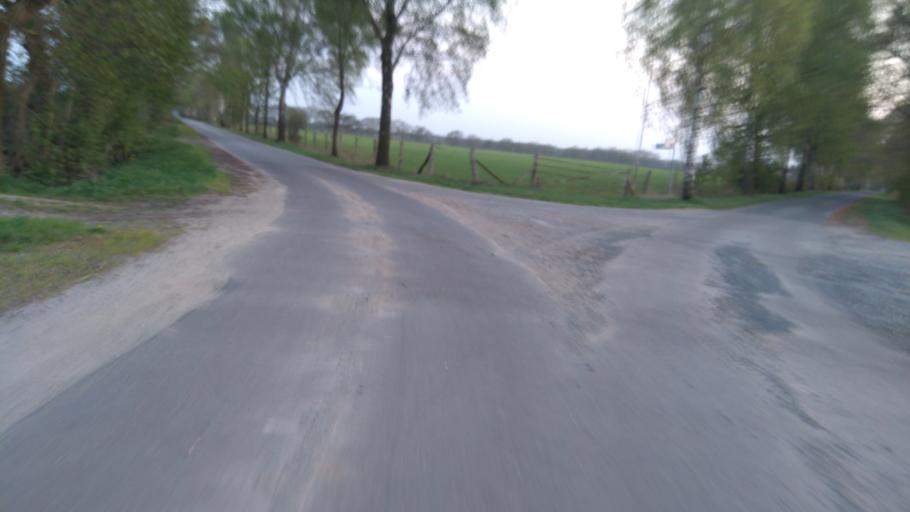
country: DE
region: Lower Saxony
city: Bargstedt
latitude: 53.4865
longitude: 9.4791
